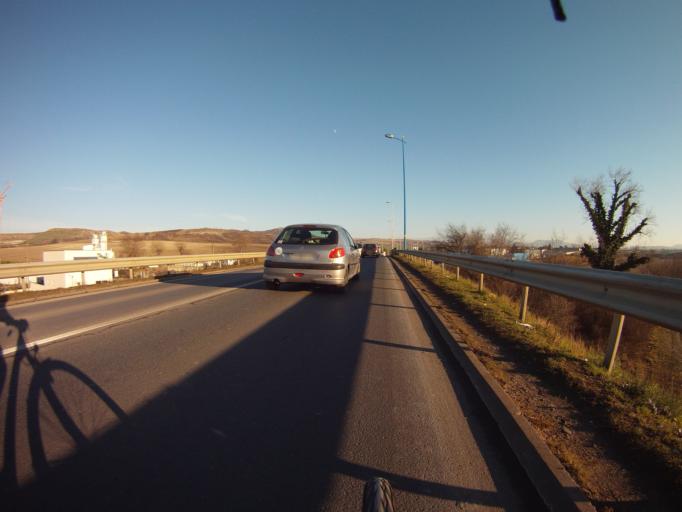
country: FR
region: Auvergne
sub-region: Departement du Puy-de-Dome
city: Perignat-les-Sarlieve
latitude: 45.7558
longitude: 3.1534
